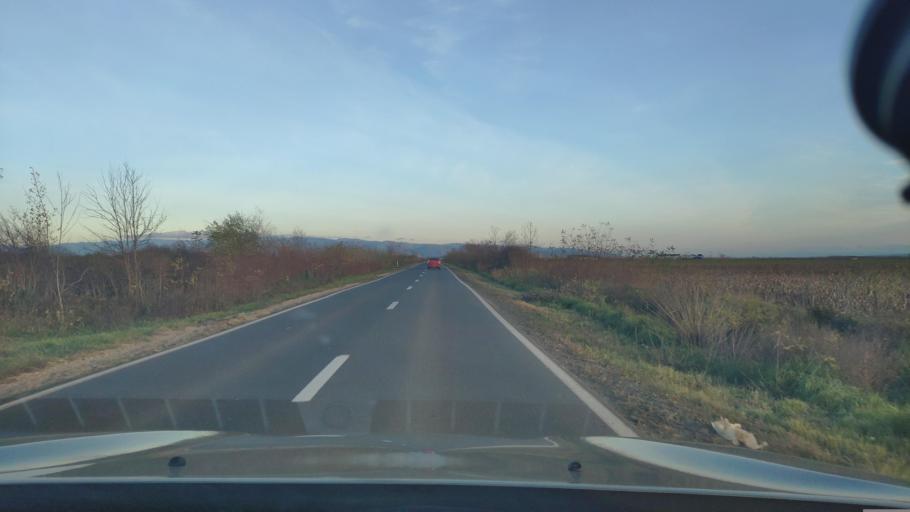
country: RO
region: Satu Mare
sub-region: Comuna Mediesu Aurit
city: Potau
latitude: 47.7722
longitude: 23.1318
